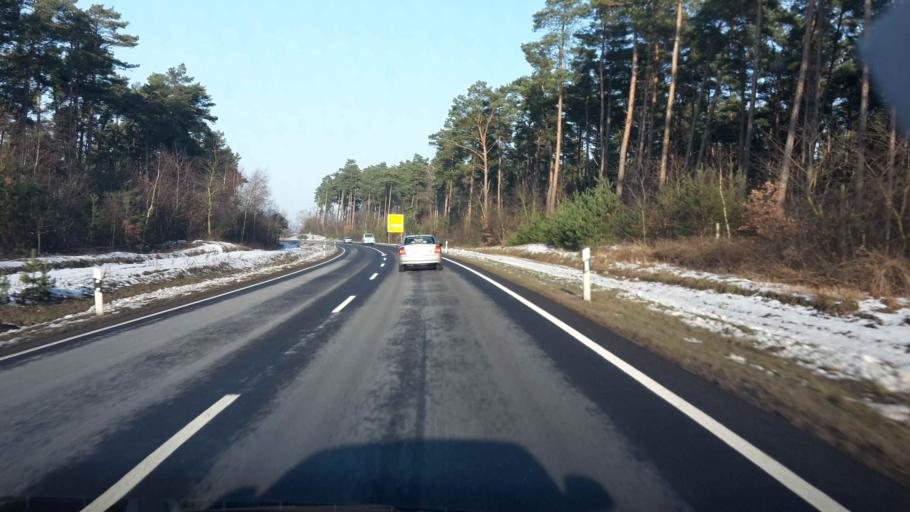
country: DE
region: Brandenburg
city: Perleberg
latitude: 53.0566
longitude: 11.8318
